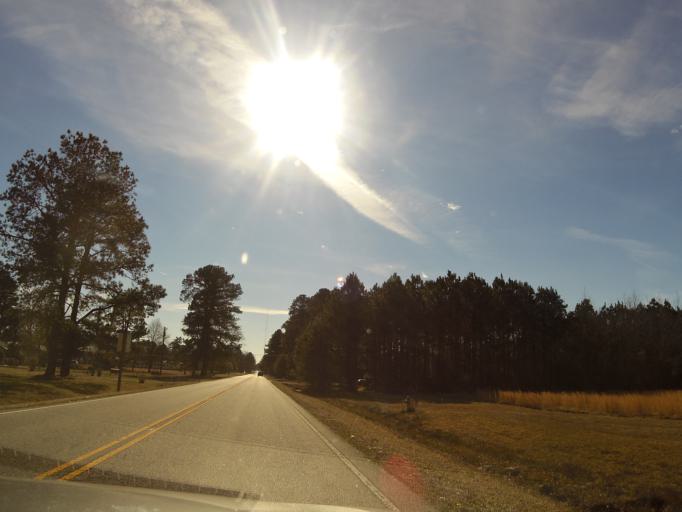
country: US
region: Virginia
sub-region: Isle of Wight County
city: Windsor
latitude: 36.8223
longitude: -76.7462
